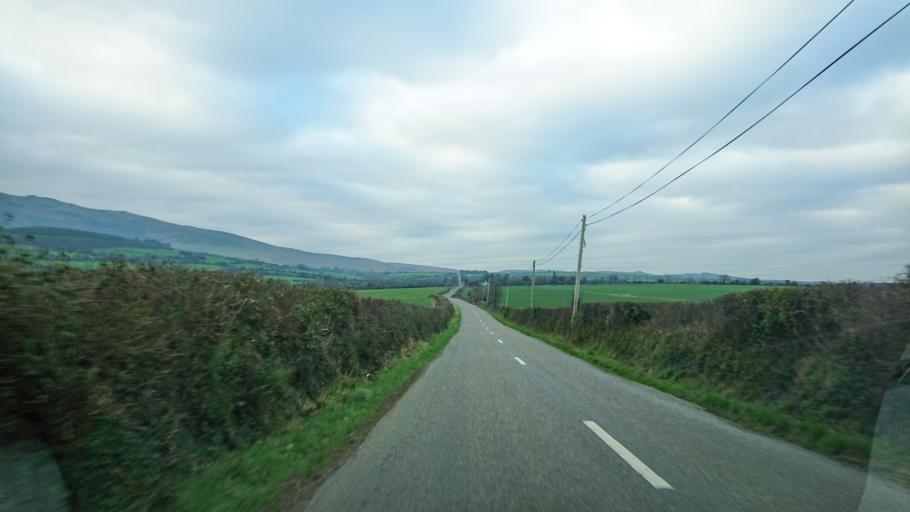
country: IE
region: Munster
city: Carrick-on-Suir
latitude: 52.3142
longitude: -7.5325
